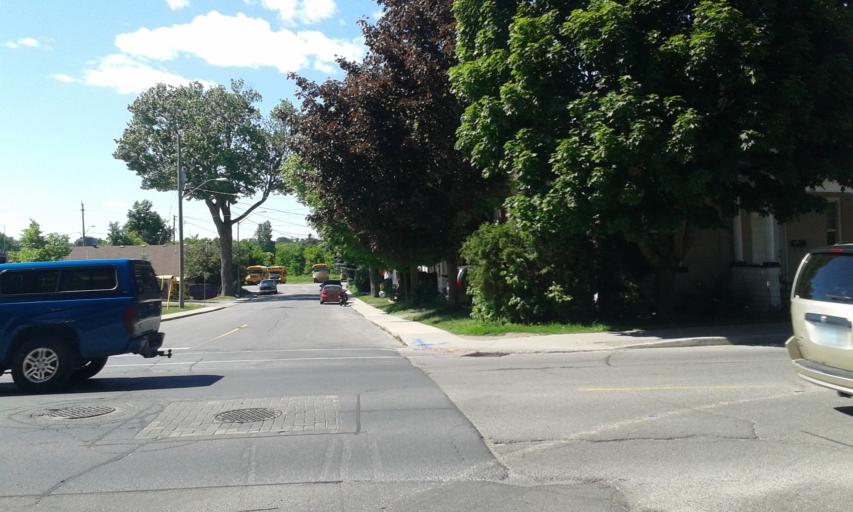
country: CA
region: Ontario
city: Brockville
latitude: 44.5923
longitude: -75.6867
